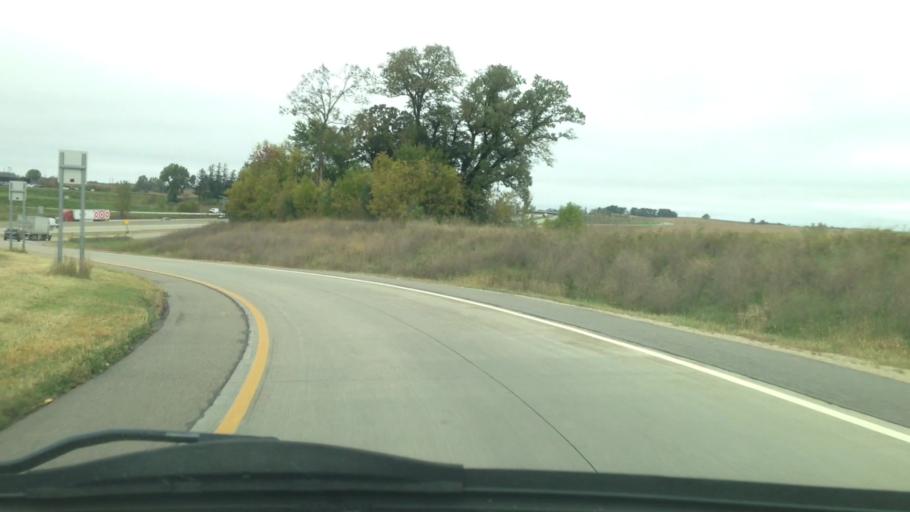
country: US
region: Minnesota
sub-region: Olmsted County
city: Oronoco
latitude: 44.0956
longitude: -92.5097
